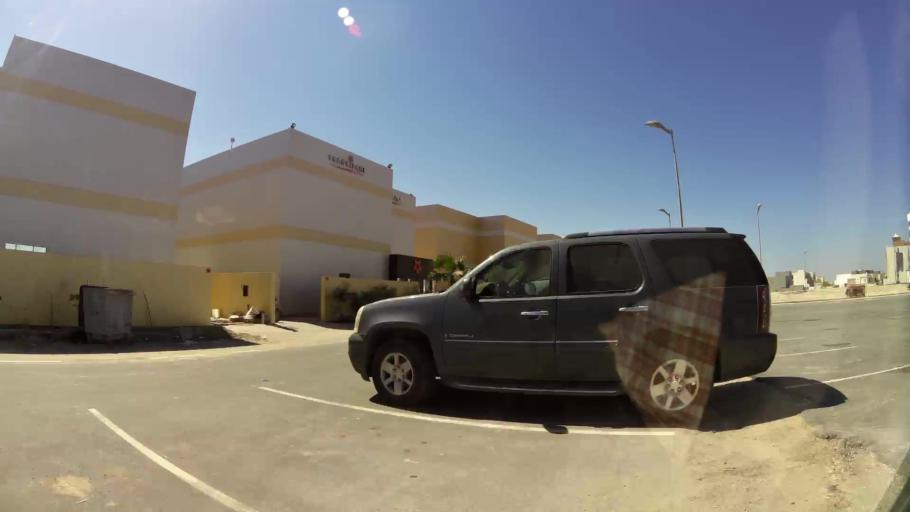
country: BH
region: Muharraq
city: Al Hadd
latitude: 26.2934
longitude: 50.6599
